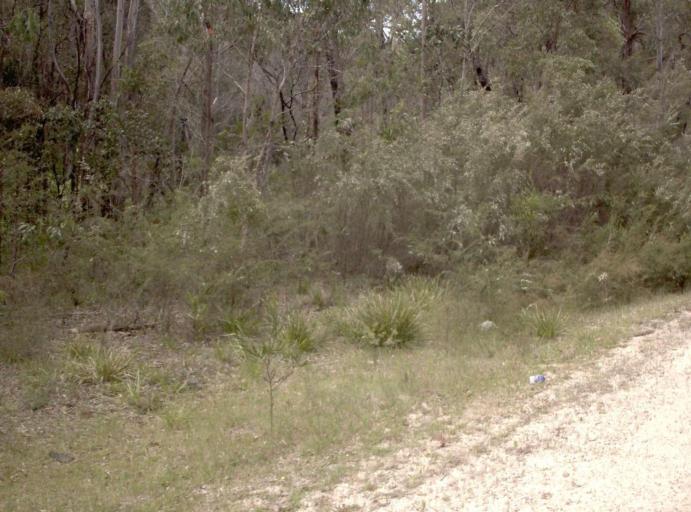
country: AU
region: New South Wales
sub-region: Bega Valley
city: Eden
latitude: -37.4054
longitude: 149.6642
